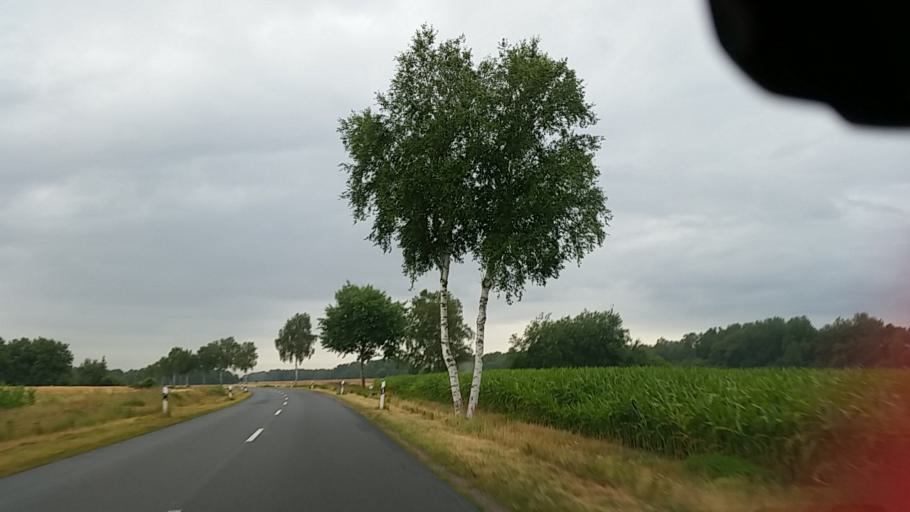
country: DE
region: Lower Saxony
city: Schoneworde
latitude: 52.5918
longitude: 10.6813
